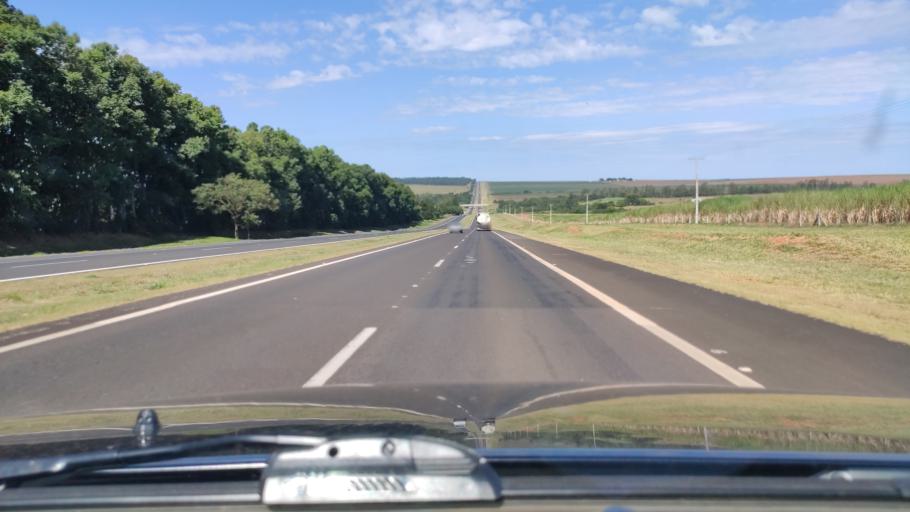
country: BR
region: Sao Paulo
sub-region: Rancharia
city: Rancharia
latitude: -22.4083
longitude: -51.0551
